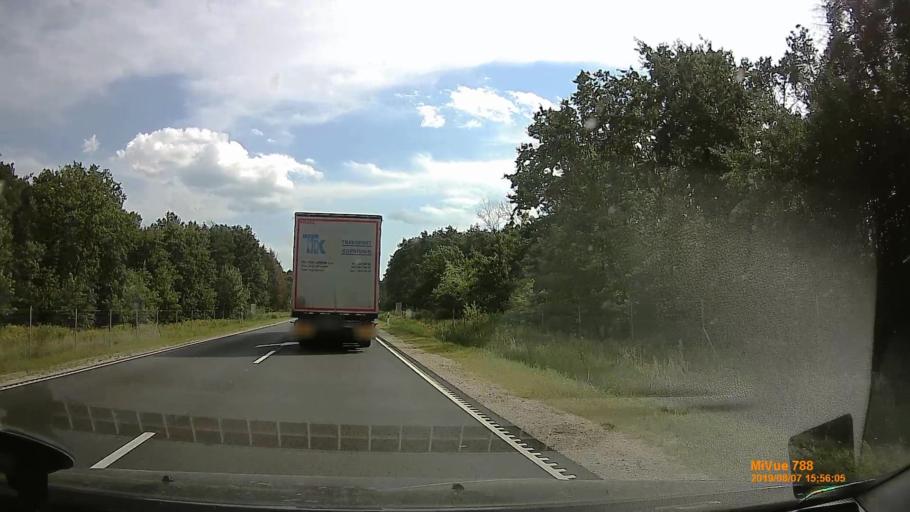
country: HU
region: Vas
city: Kormend
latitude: 47.0655
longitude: 16.6166
